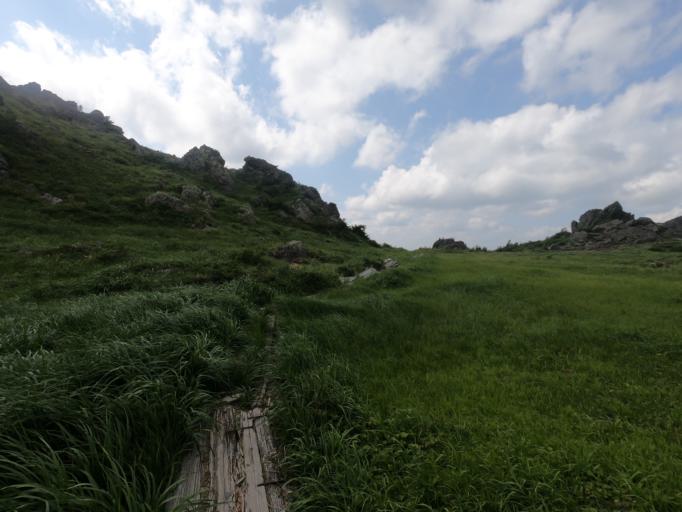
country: JP
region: Akita
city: Yuzawa
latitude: 38.9748
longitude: 140.7747
